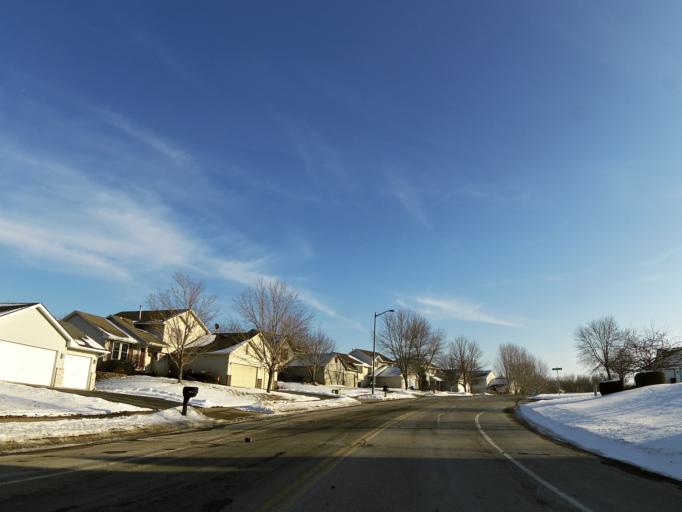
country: US
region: Minnesota
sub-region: Scott County
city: Savage
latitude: 44.7395
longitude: -93.3517
